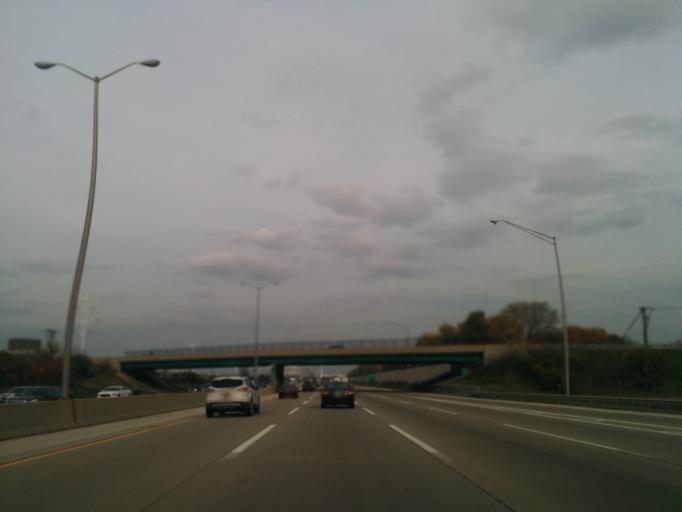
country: US
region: Illinois
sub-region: DuPage County
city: Oakbrook Terrace
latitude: 41.8392
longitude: -87.9920
